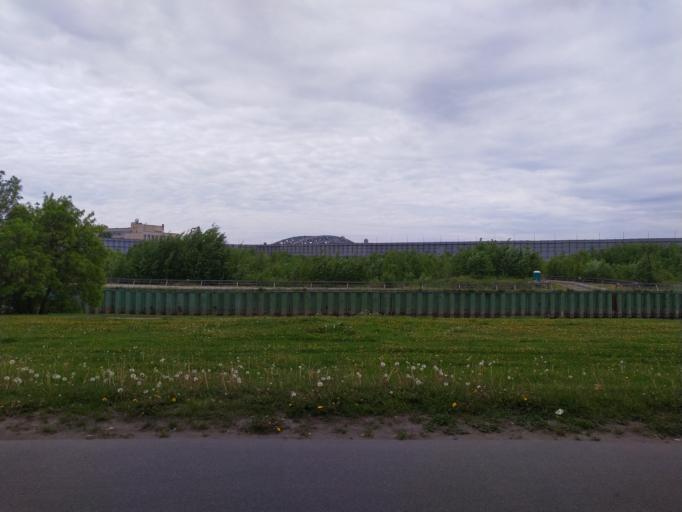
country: RU
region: St.-Petersburg
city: Centralniy
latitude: 59.9445
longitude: 30.4103
